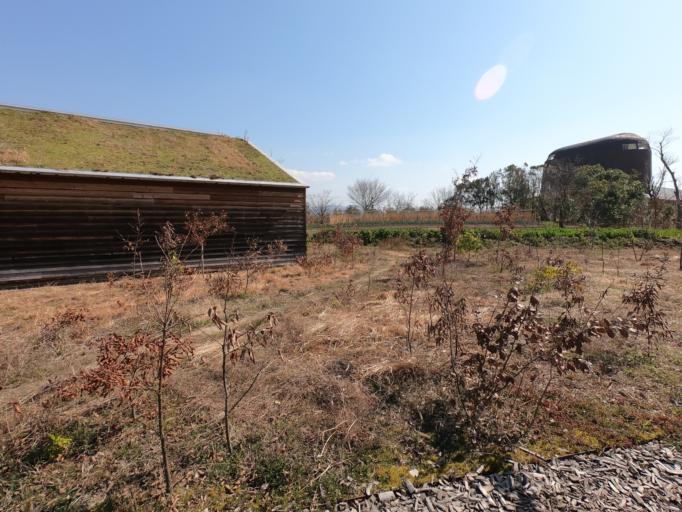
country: JP
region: Shiga Prefecture
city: Omihachiman
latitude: 35.1573
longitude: 136.0729
